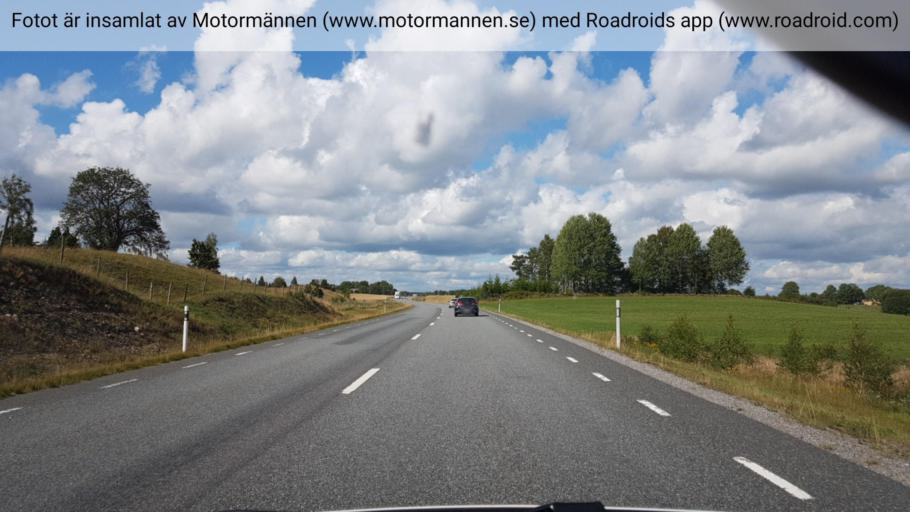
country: SE
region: Vaestra Goetaland
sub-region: Falkopings Kommun
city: Falkoeping
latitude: 57.9730
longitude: 13.5296
